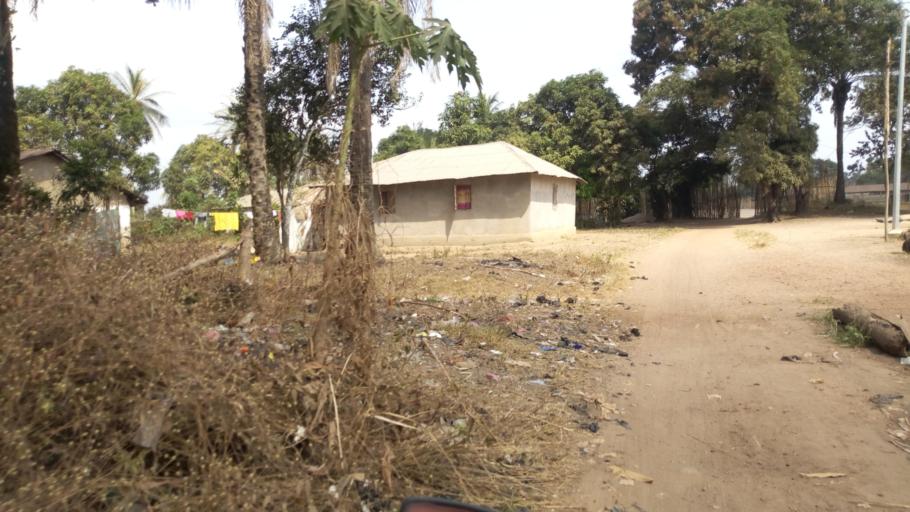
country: SL
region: Southern Province
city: Mogbwemo
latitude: 7.7887
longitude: -12.3007
